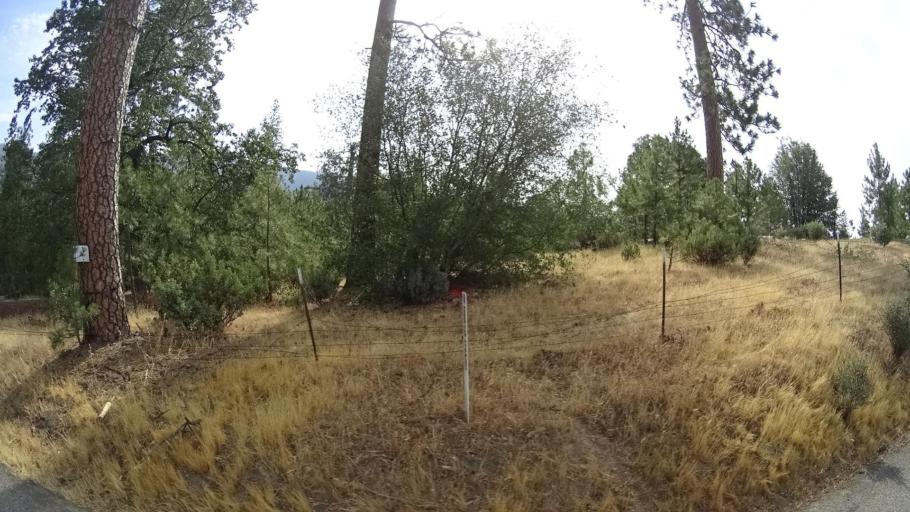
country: US
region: California
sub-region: Mariposa County
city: Midpines
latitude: 37.4862
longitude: -119.8117
